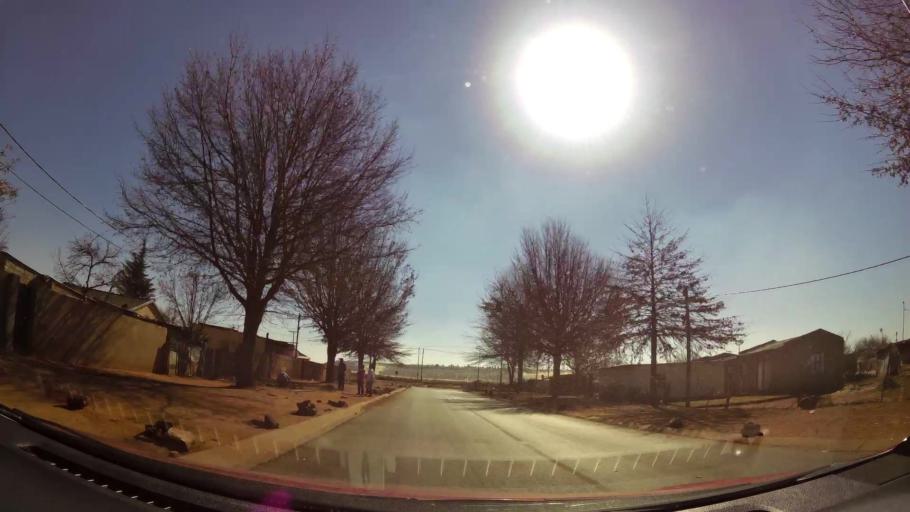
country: ZA
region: Gauteng
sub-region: City of Johannesburg Metropolitan Municipality
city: Soweto
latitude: -26.2163
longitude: 27.8326
